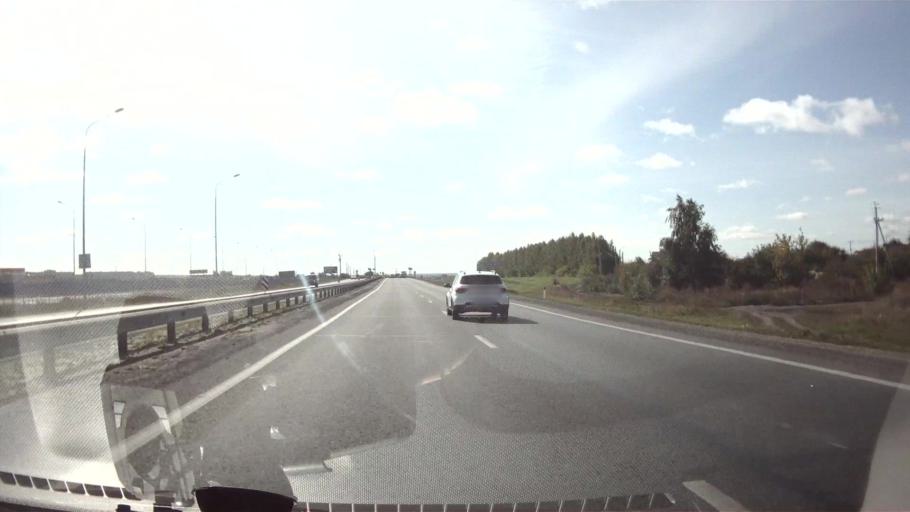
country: RU
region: Ulyanovsk
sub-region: Ulyanovskiy Rayon
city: Ulyanovsk
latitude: 54.2810
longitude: 48.2587
